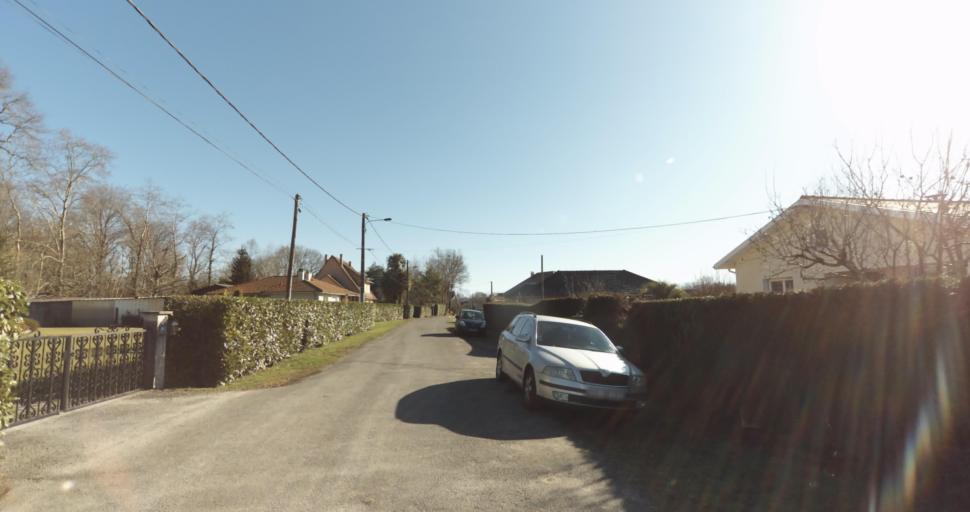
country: FR
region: Aquitaine
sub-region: Departement des Pyrenees-Atlantiques
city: Buros
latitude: 43.3305
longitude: -0.2885
